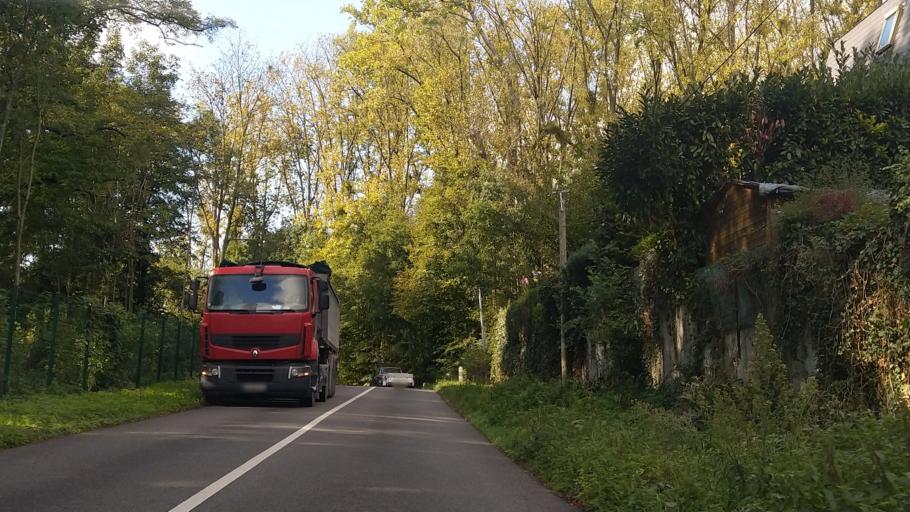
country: FR
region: Ile-de-France
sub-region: Departement du Val-d'Oise
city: Baillet-en-France
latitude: 49.0664
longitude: 2.2992
